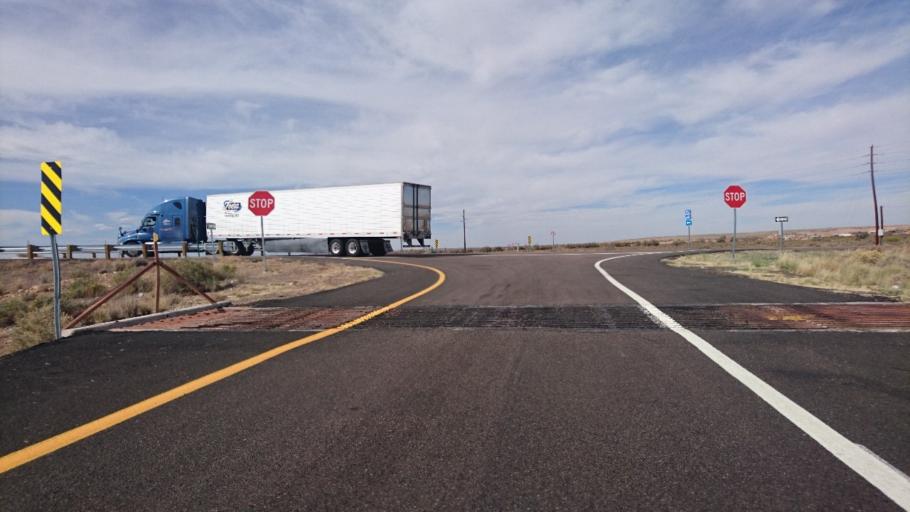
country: US
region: Arizona
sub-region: Navajo County
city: Winslow
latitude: 35.0103
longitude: -110.6401
